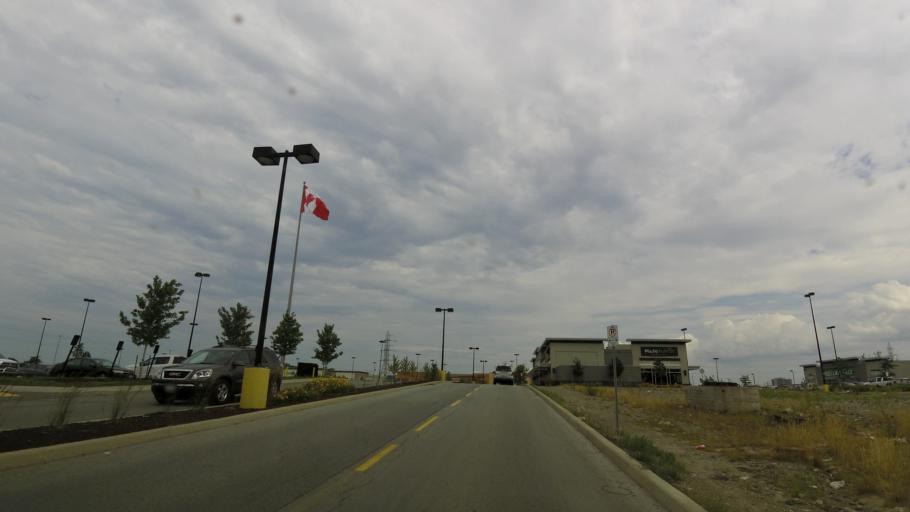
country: CA
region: Ontario
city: Hamilton
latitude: 43.2425
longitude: -79.7574
